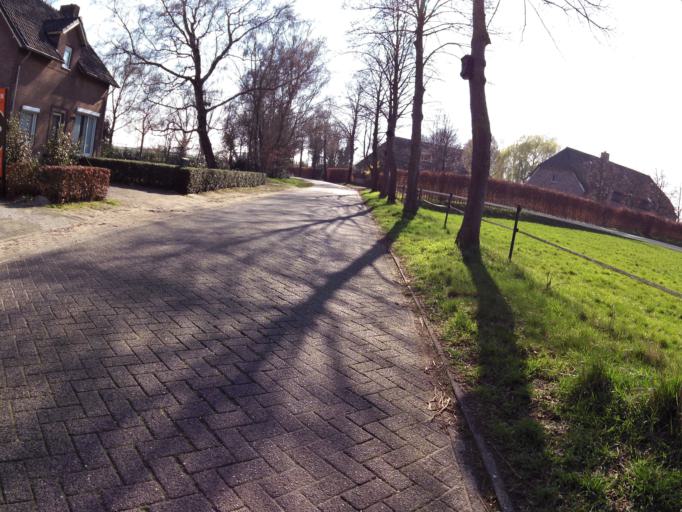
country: NL
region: North Brabant
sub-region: Gemeente Sint-Michielsgestel
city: Sint-Michielsgestel
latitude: 51.6745
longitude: 5.3896
